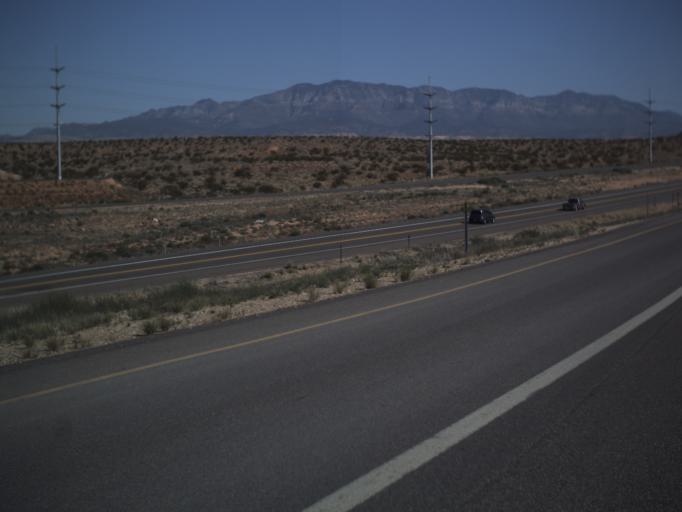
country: US
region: Utah
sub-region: Washington County
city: Washington
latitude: 37.0148
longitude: -113.4938
